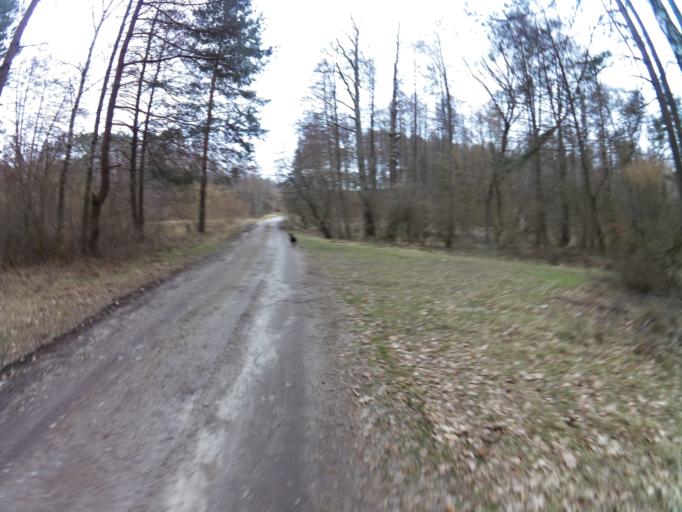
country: PL
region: West Pomeranian Voivodeship
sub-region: Powiat mysliborski
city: Debno
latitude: 52.7512
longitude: 14.7870
